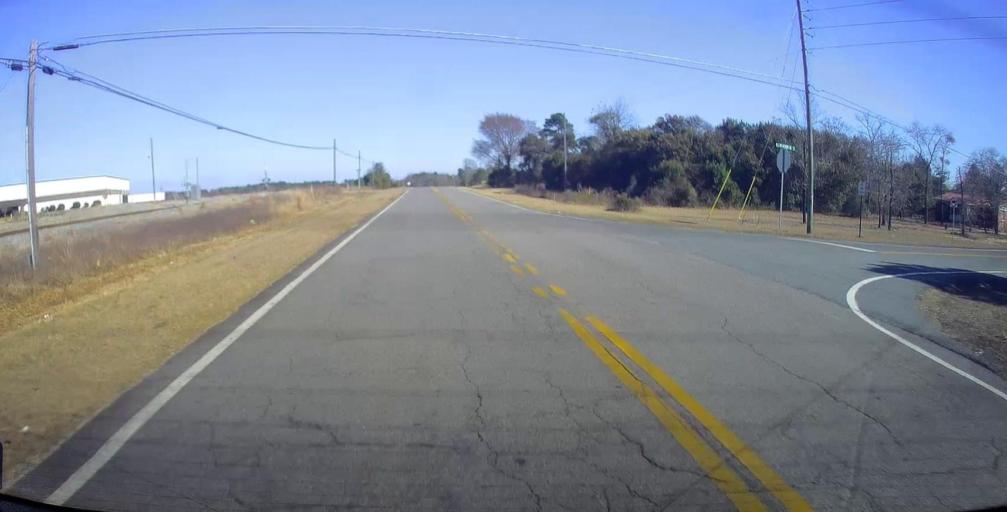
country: US
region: Georgia
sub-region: Taylor County
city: Butler
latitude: 32.5640
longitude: -84.2590
